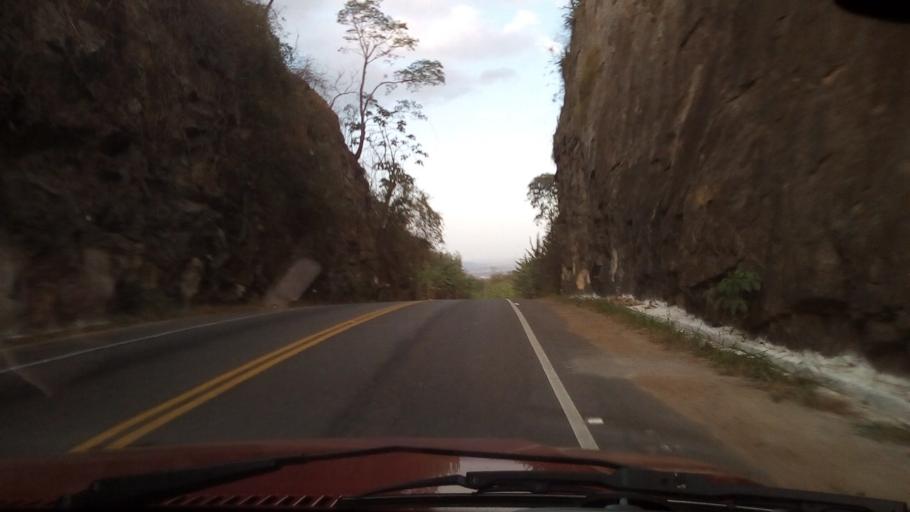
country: BR
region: Paraiba
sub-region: Bananeiras
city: Solanea
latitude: -6.7472
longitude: -35.5640
